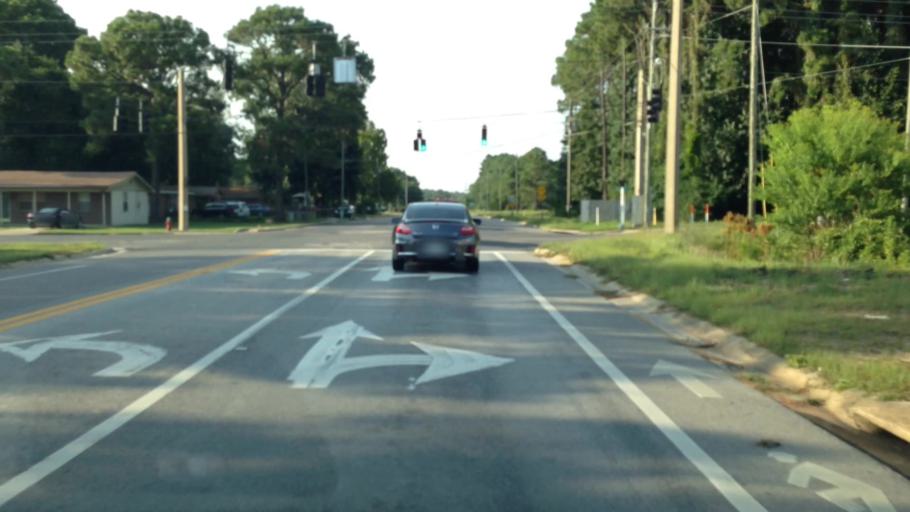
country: US
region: Florida
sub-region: Okaloosa County
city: Mary Esther
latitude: 30.4242
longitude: -86.6673
